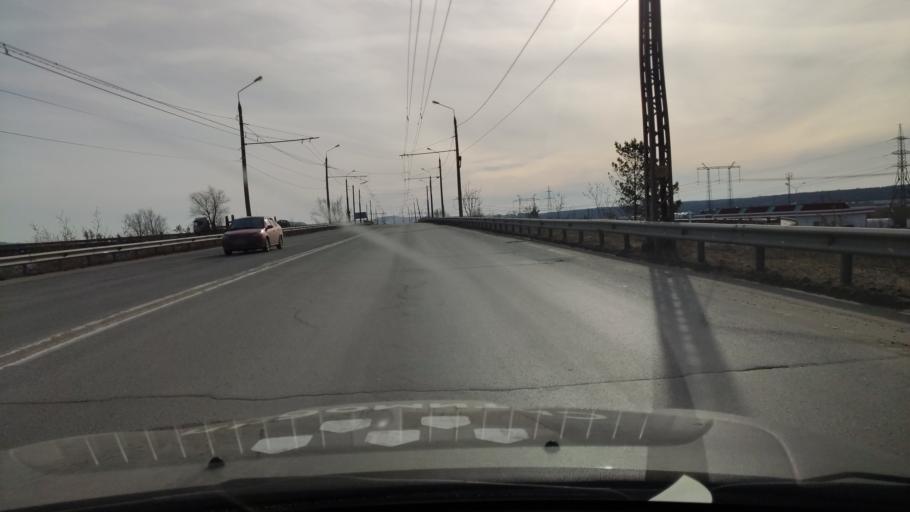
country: RU
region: Samara
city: Zhigulevsk
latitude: 53.5195
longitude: 49.5380
